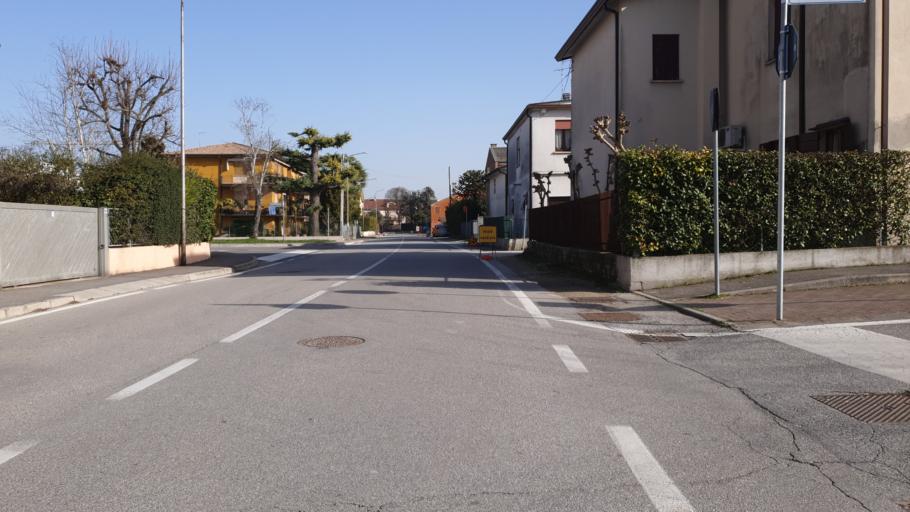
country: IT
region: Veneto
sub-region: Provincia di Padova
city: Vigodarzere
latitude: 45.4572
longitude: 11.8857
